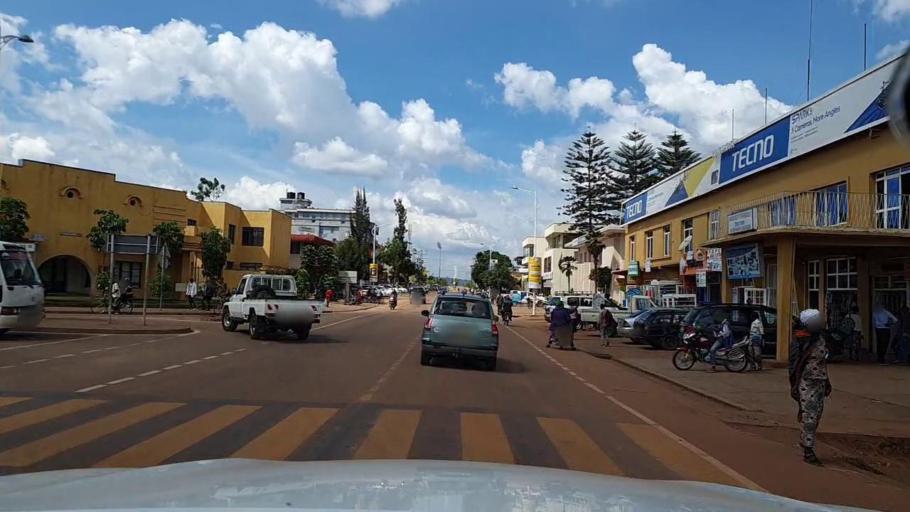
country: RW
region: Southern Province
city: Butare
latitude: -2.6033
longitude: 29.7414
